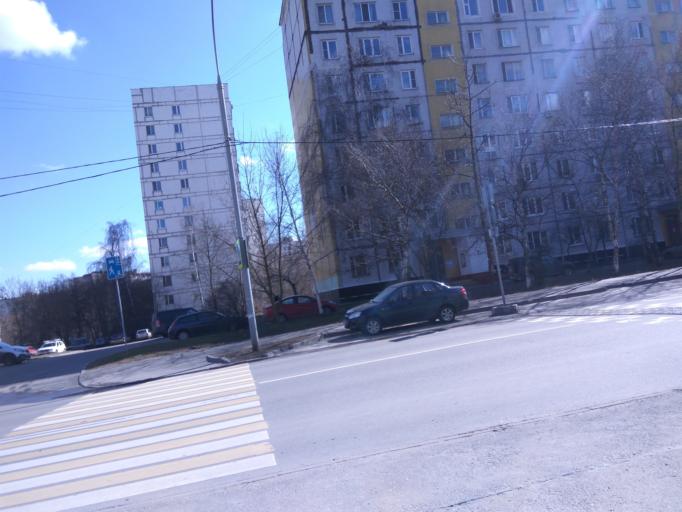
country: RU
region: Moscow
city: Ivanovskoye
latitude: 55.7822
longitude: 37.8339
